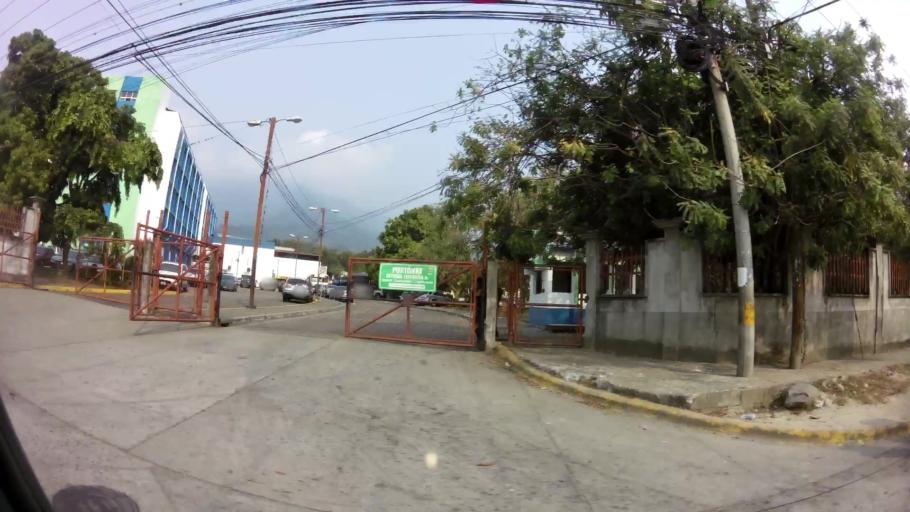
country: HN
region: Cortes
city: El Zapotal del Norte
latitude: 15.5244
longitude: -88.0404
